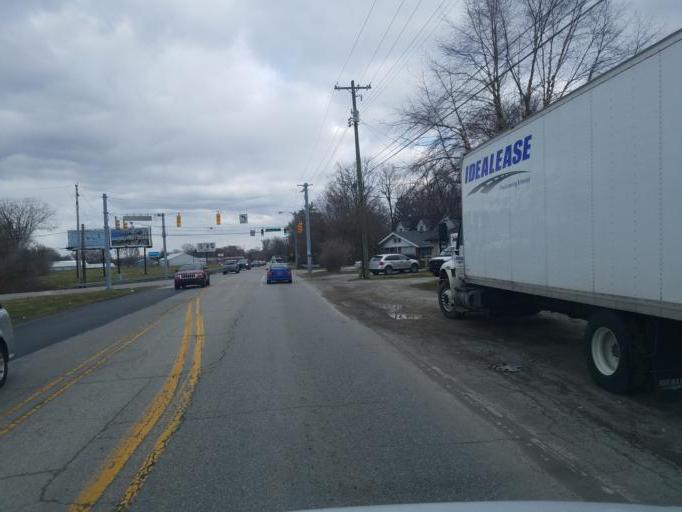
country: US
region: Indiana
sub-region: Marion County
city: Speedway
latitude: 39.7641
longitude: -86.2352
